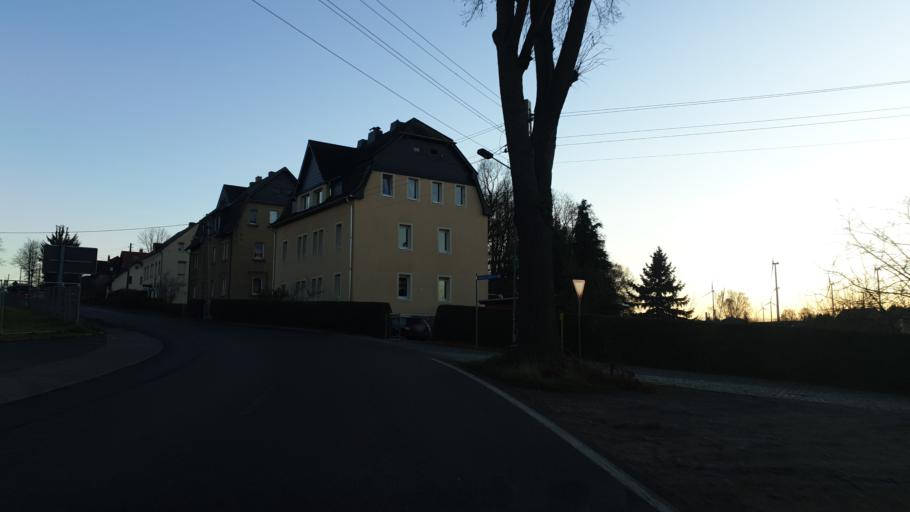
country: DE
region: Saxony
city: Oberlungwitz
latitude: 50.7808
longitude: 12.7012
